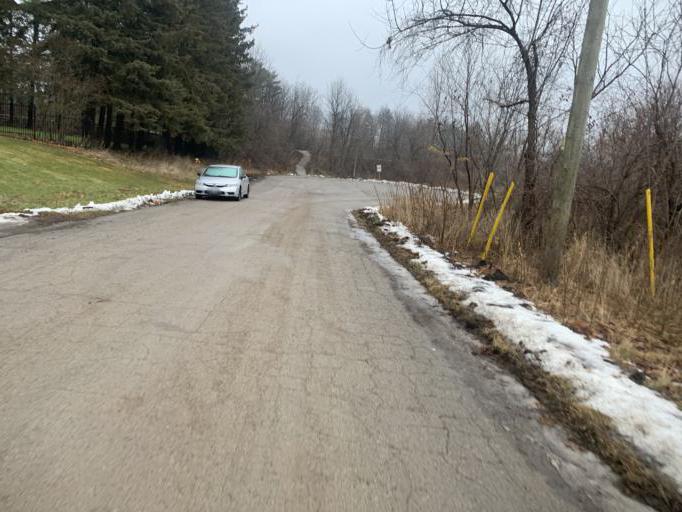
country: CA
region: Ontario
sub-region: Halton
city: Milton
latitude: 43.6610
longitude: -79.9318
